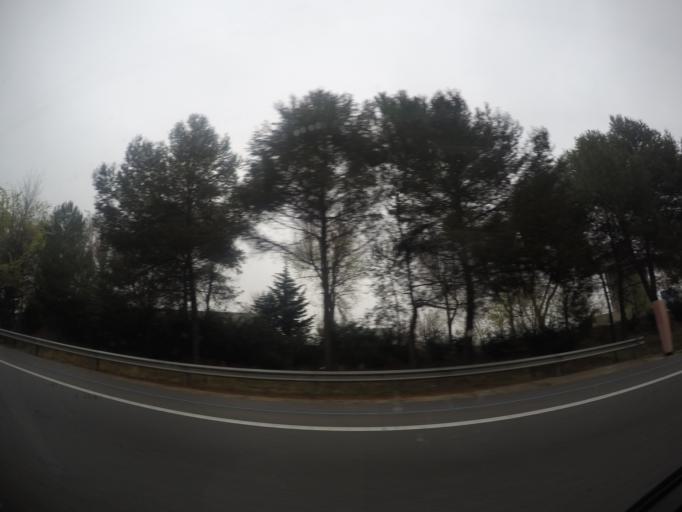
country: ES
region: Catalonia
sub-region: Provincia de Barcelona
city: Subirats
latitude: 41.4225
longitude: 1.8182
